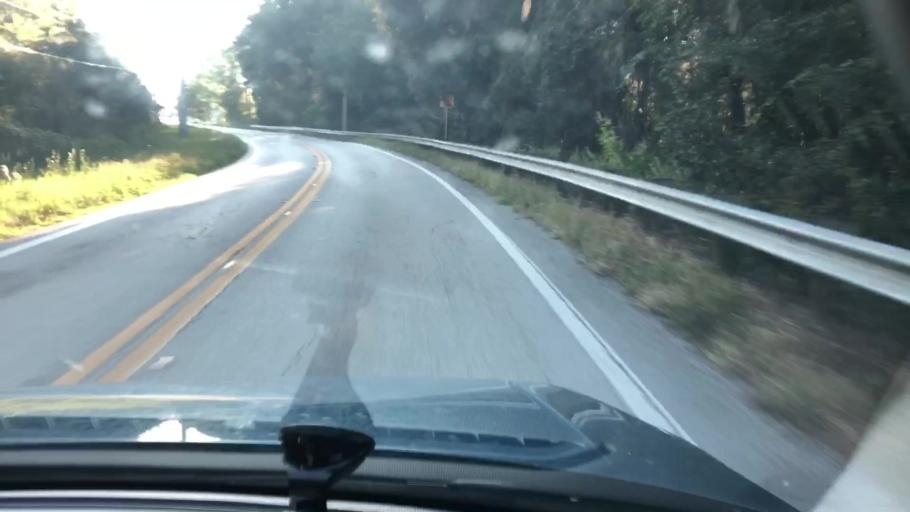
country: US
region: Florida
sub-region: Polk County
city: Gibsonia
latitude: 28.1573
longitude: -81.9146
